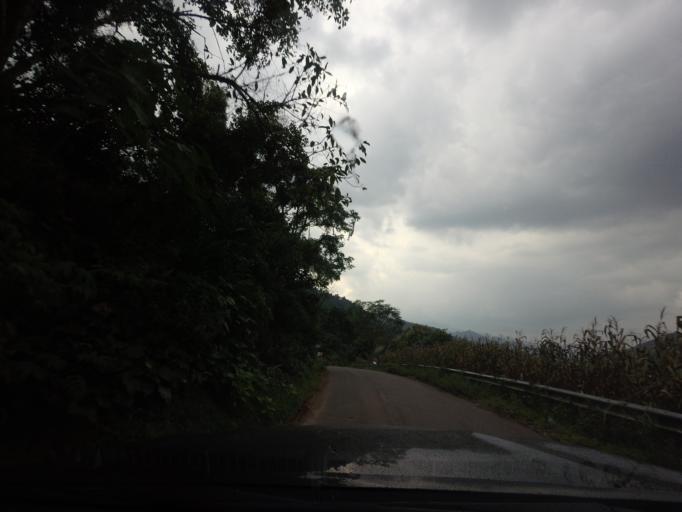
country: TH
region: Nan
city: Bo Kluea
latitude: 19.3275
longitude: 101.1705
